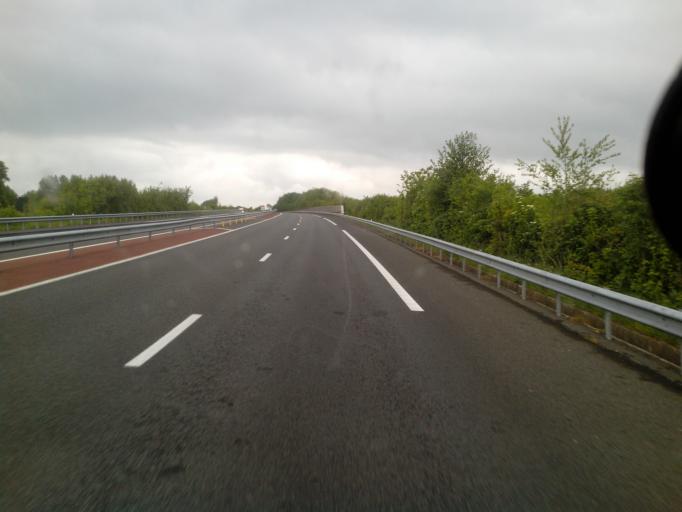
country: FR
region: Lower Normandy
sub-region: Departement de la Manche
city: Villedieu-les-Poeles
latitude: 48.7836
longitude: -1.2669
